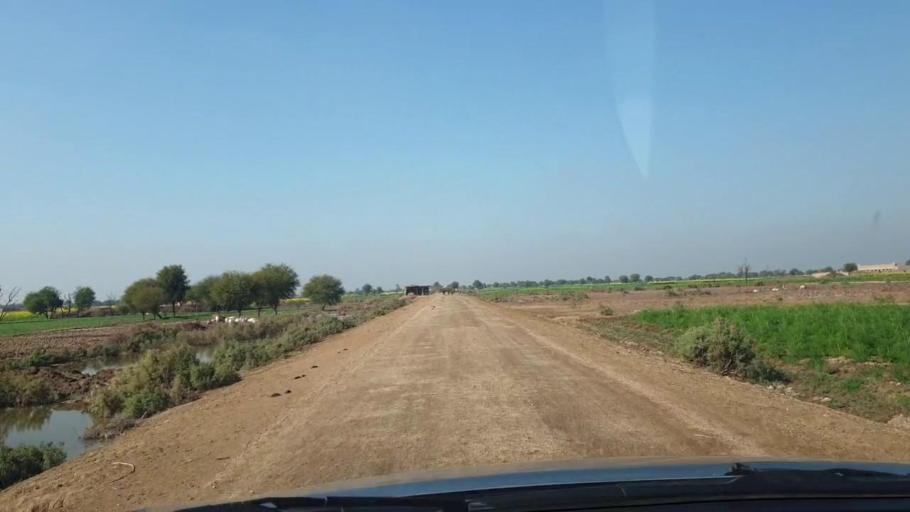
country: PK
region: Sindh
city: Jhol
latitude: 25.8808
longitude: 68.9153
